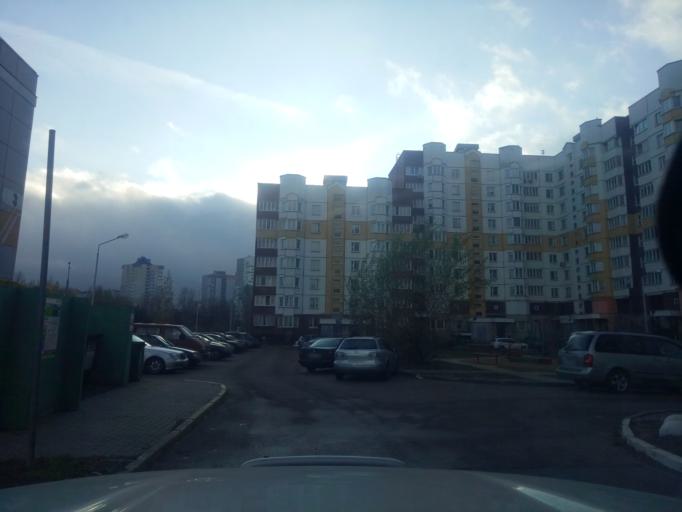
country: BY
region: Minsk
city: Novoye Medvezhino
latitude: 53.8779
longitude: 27.4833
